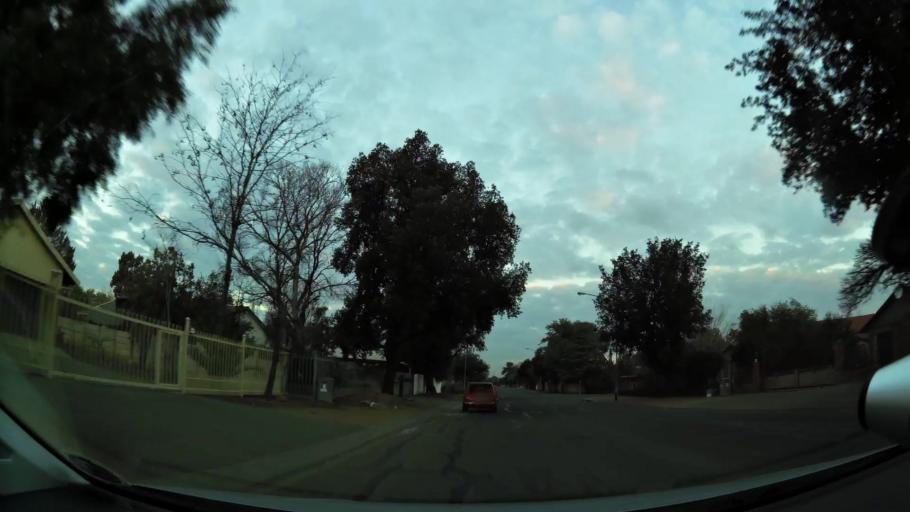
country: ZA
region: Orange Free State
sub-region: Mangaung Metropolitan Municipality
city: Bloemfontein
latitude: -29.1677
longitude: 26.1881
